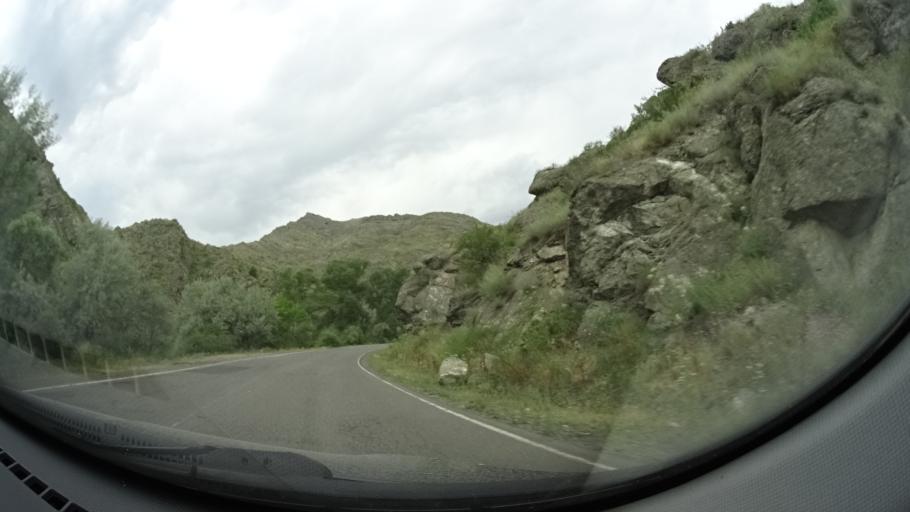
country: GE
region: Samtskhe-Javakheti
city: Akhaltsikhe
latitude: 41.6163
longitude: 43.1056
